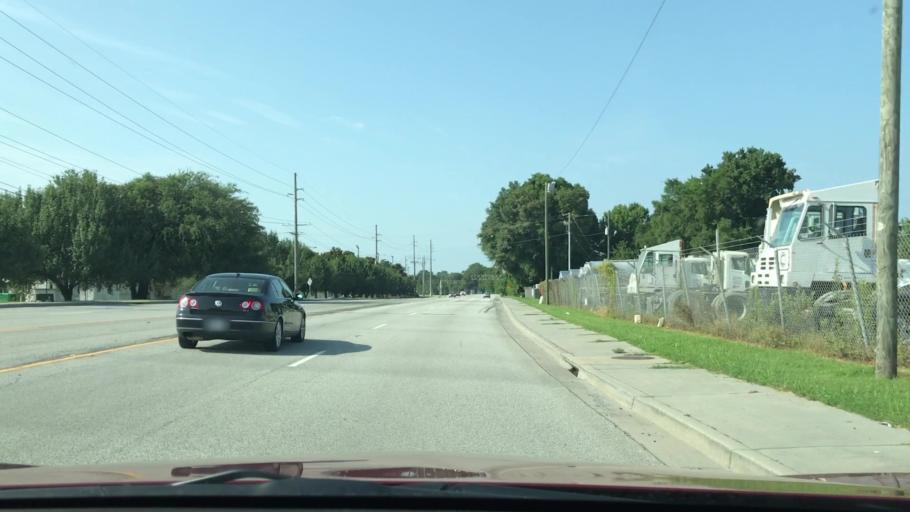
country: US
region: South Carolina
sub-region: Charleston County
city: North Charleston
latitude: 32.8869
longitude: -79.9730
